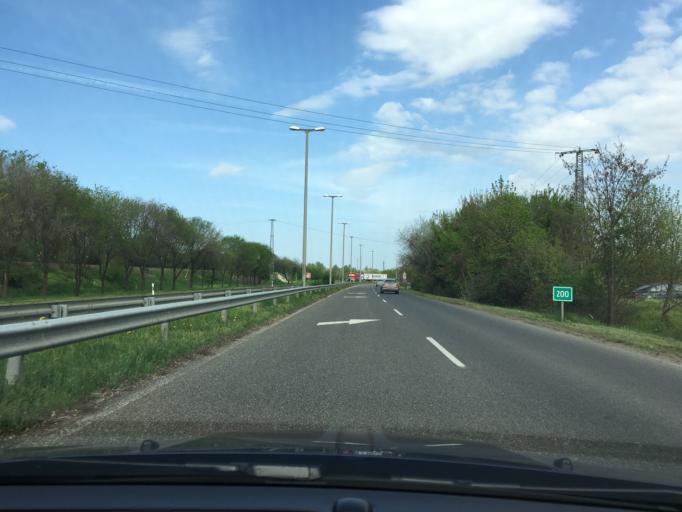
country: HU
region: Csongrad
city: Hodmezovasarhely
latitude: 46.4056
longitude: 20.3202
